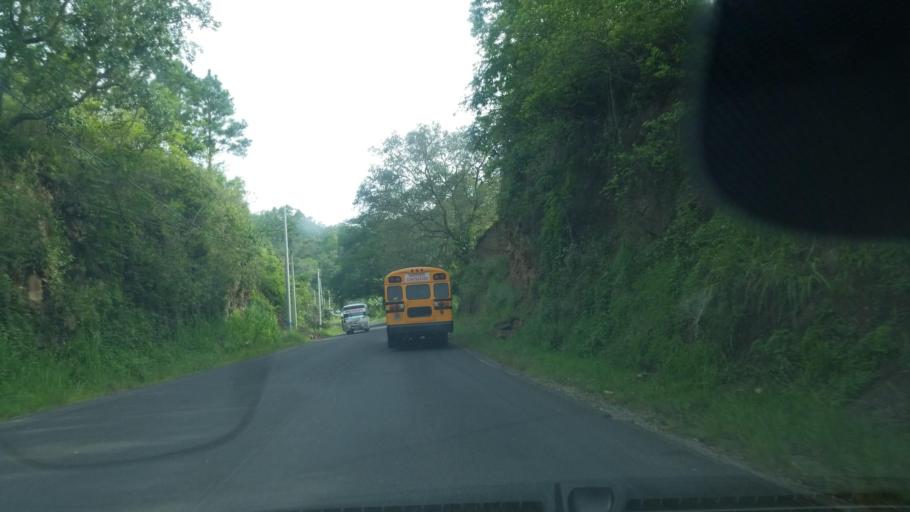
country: HN
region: Santa Barbara
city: Trinidad
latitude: 15.1866
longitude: -88.2751
